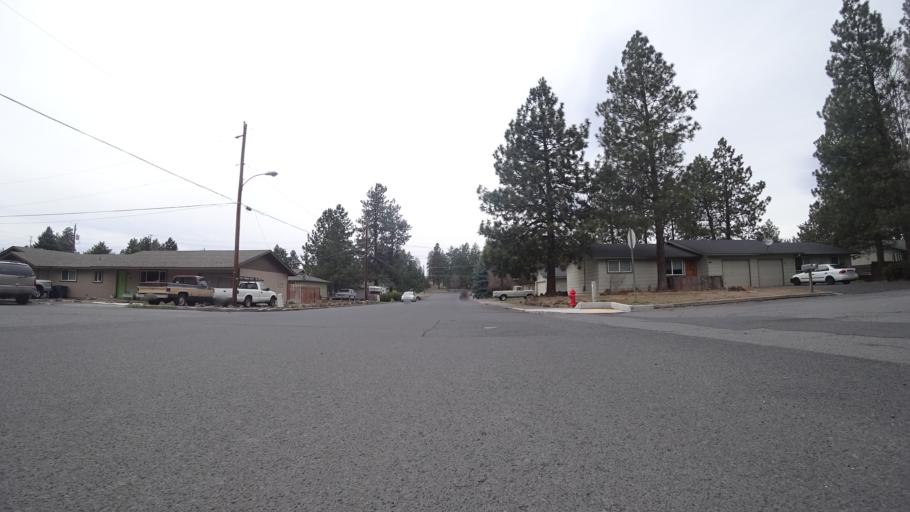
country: US
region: Oregon
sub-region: Deschutes County
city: Bend
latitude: 44.0460
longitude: -121.2820
